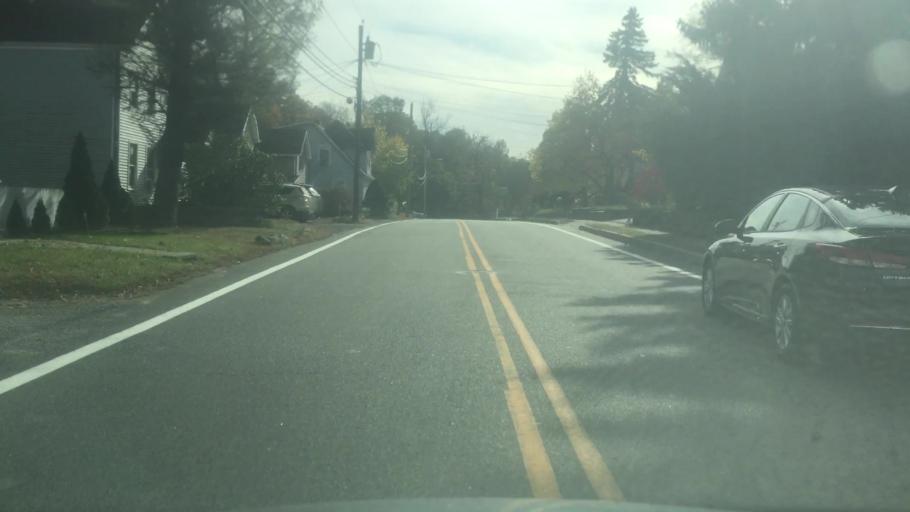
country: US
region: New Jersey
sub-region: Morris County
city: Butler
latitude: 41.0117
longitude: -74.3353
